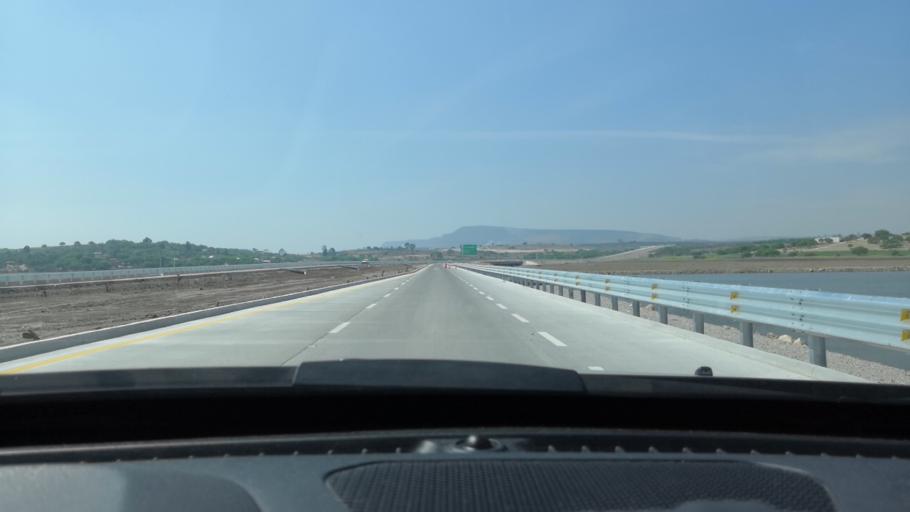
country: MX
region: Guanajuato
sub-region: Purisima del Rincon
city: Potrerillos (Guanajal)
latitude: 21.0777
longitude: -101.8611
